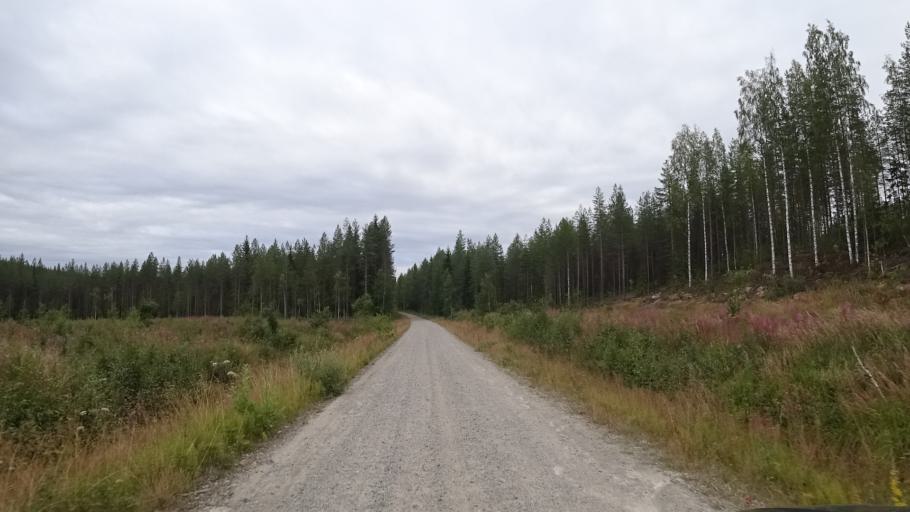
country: FI
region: North Karelia
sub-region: Joensuu
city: Ilomantsi
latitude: 63.1531
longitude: 30.6427
